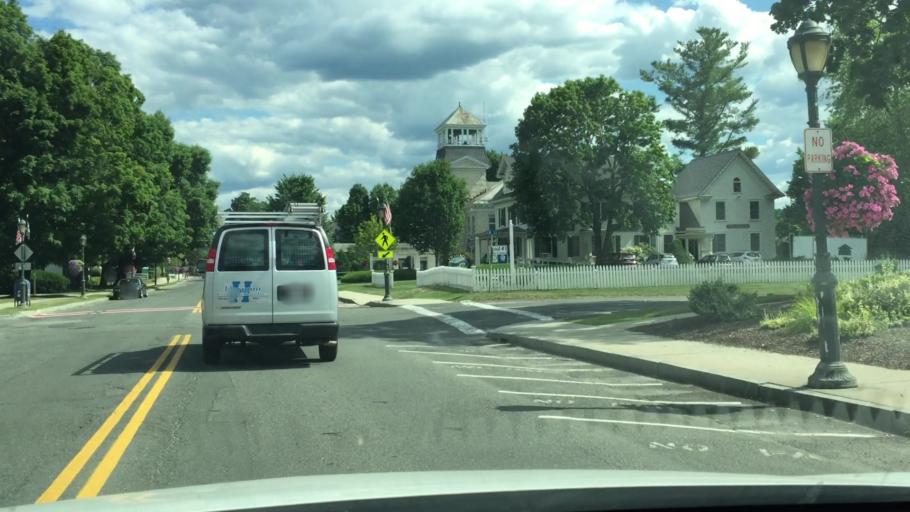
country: US
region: Massachusetts
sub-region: Berkshire County
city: Lee
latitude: 42.3090
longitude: -73.2514
